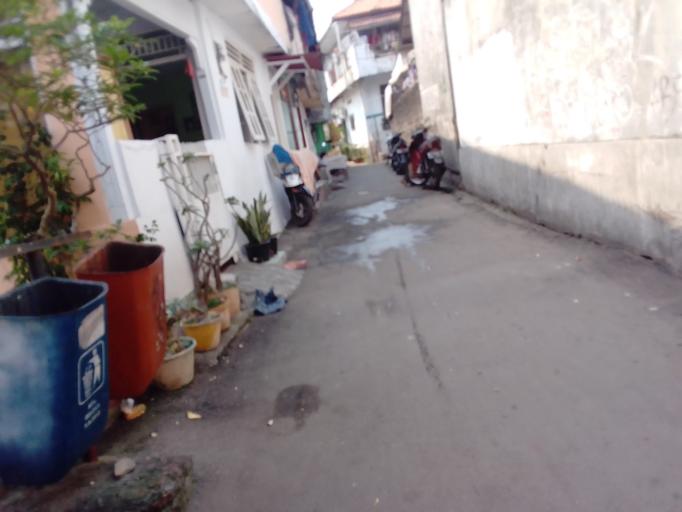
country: ID
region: Jakarta Raya
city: Jakarta
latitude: -6.2100
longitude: 106.7929
